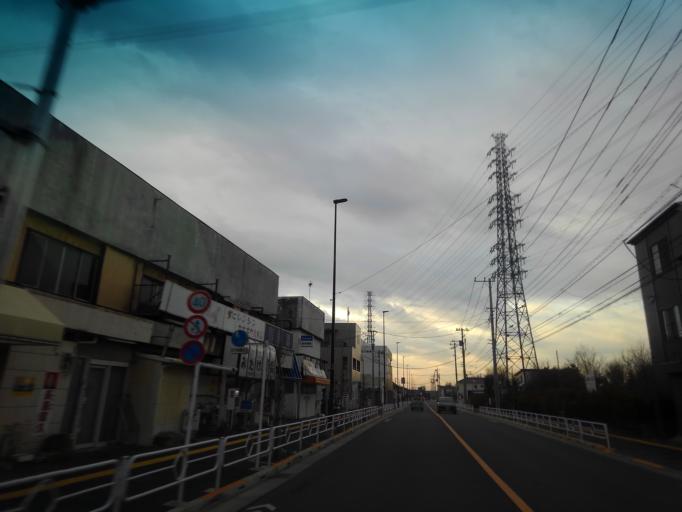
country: JP
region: Tokyo
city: Kokubunji
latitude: 35.7222
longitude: 139.4428
